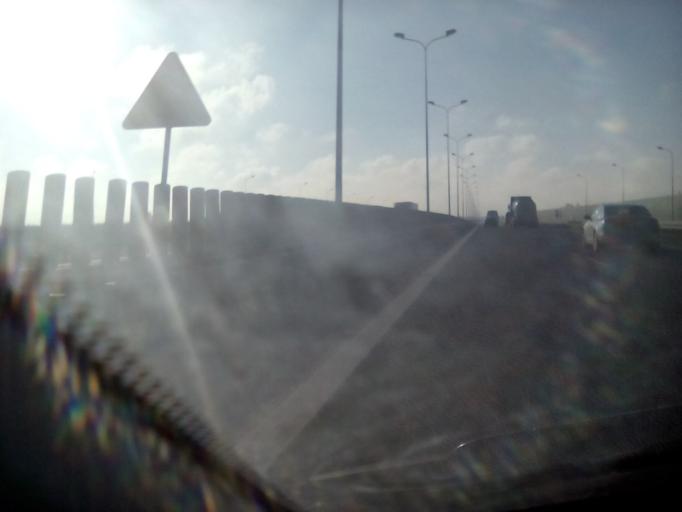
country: PL
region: Masovian Voivodeship
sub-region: Powiat grojecki
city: Grojec
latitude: 51.8272
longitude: 20.8798
